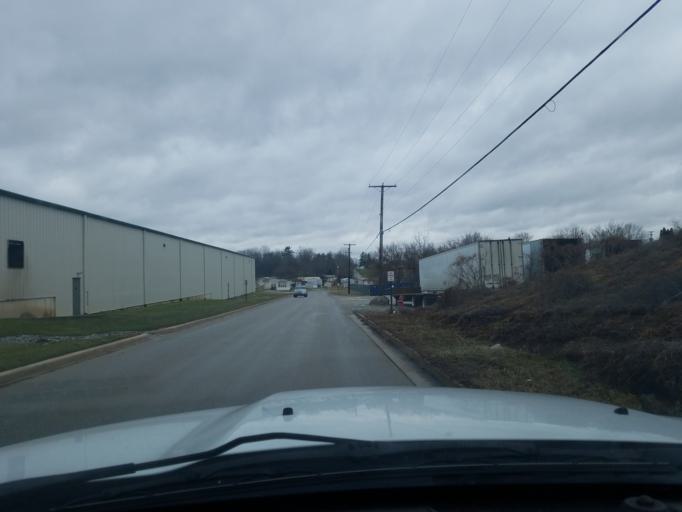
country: US
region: Indiana
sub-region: Noble County
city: Albion
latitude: 41.3927
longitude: -85.4080
